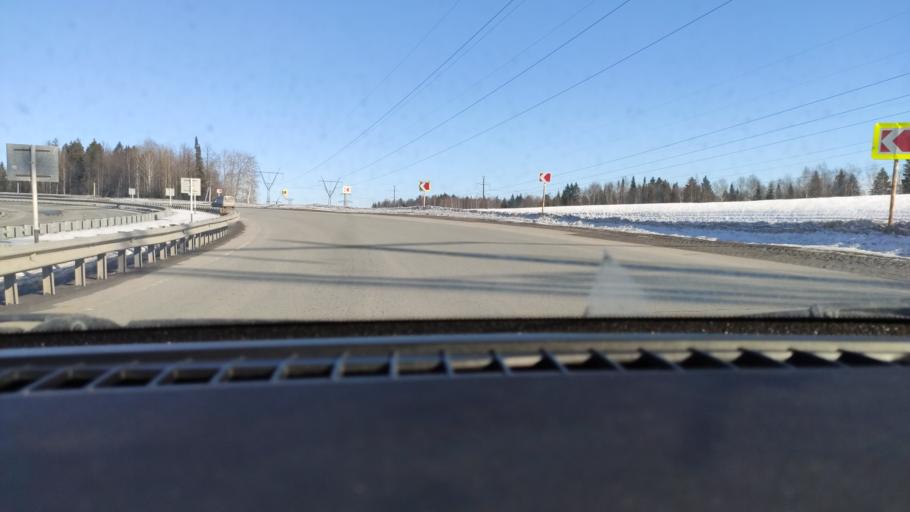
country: RU
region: Perm
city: Ferma
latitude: 57.9980
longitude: 56.3869
